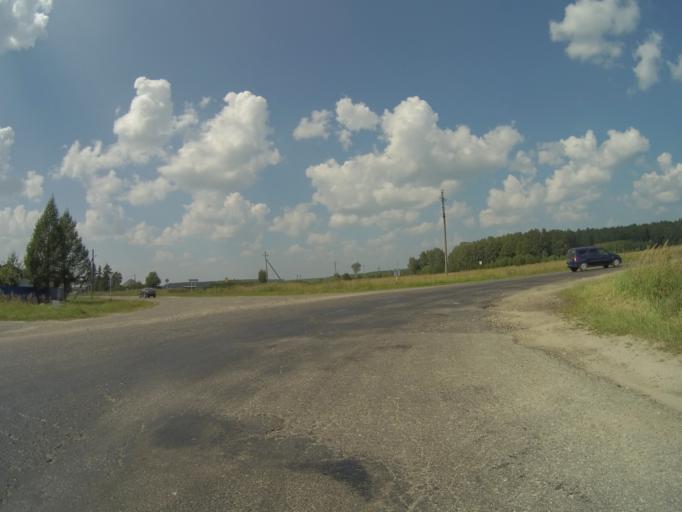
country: RU
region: Vladimir
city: Anopino
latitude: 55.6414
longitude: 40.8257
